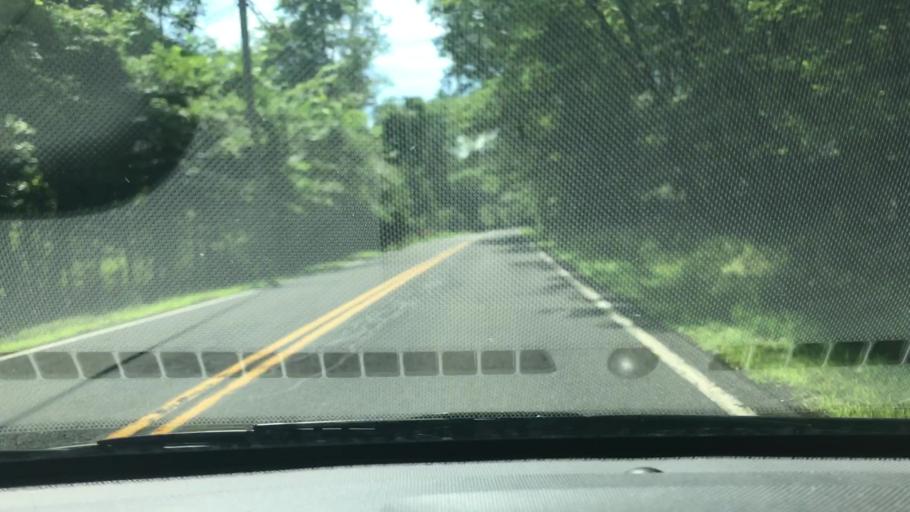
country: US
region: New York
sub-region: Ulster County
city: Shokan
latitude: 41.9166
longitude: -74.1837
